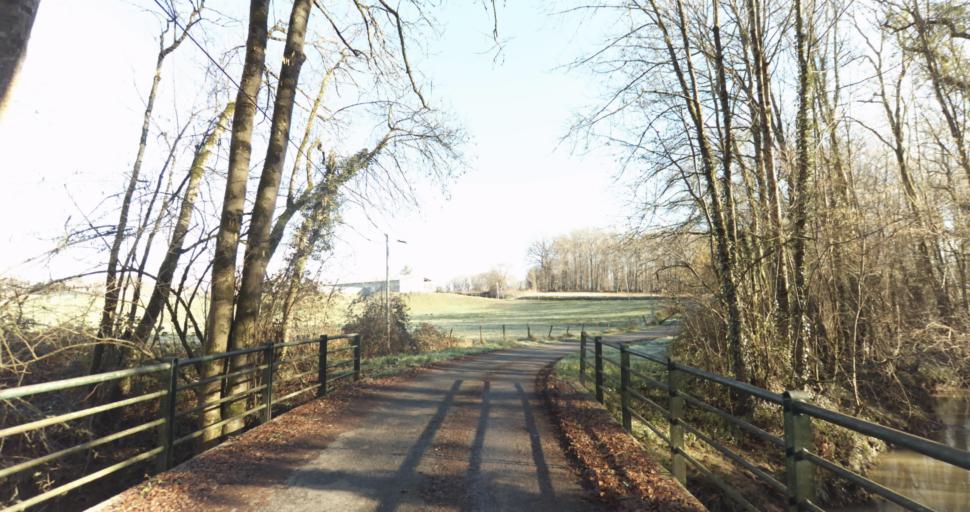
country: FR
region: Aquitaine
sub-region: Departement des Pyrenees-Atlantiques
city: Morlaas
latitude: 43.3403
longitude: -0.2457
